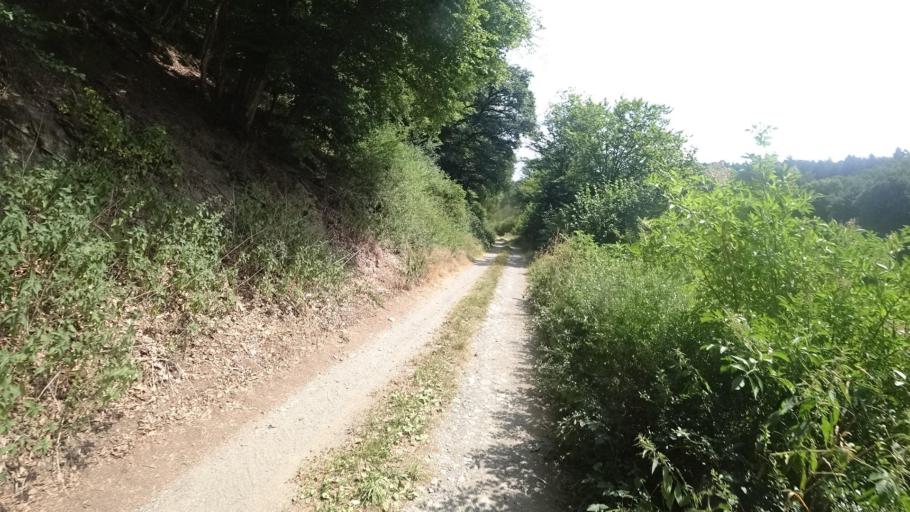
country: DE
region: Rheinland-Pfalz
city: Heckenbach
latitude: 50.4809
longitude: 7.0748
